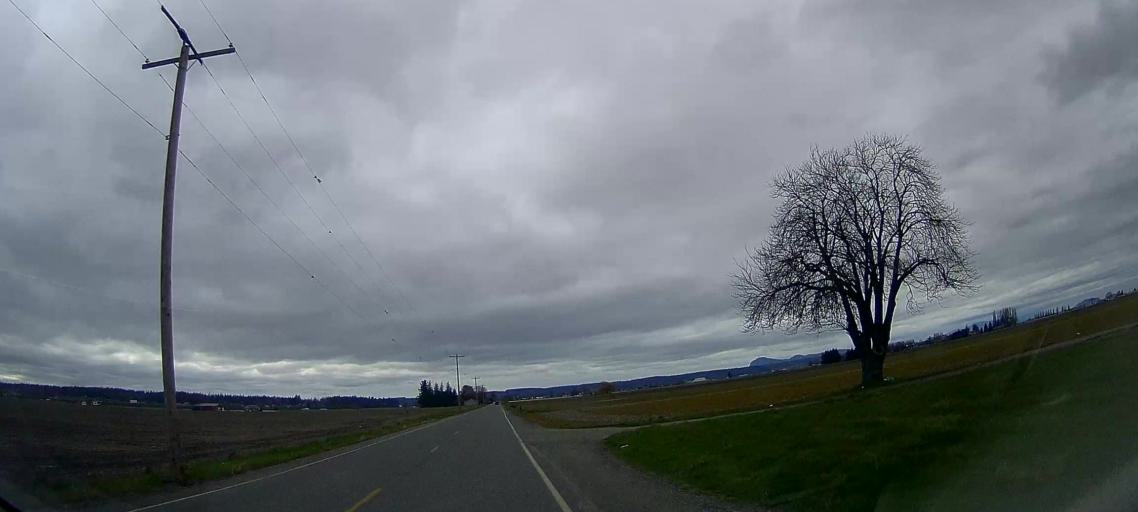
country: US
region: Washington
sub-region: Skagit County
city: Mount Vernon
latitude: 48.3993
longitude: -122.4118
